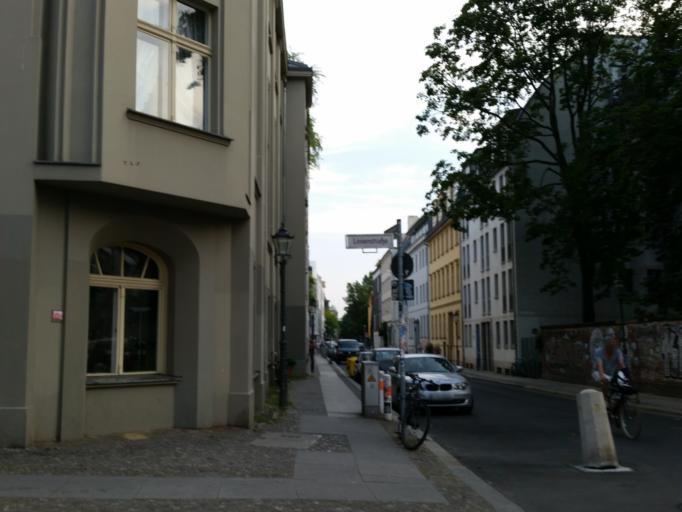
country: DE
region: Berlin
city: Berlin
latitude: 52.5288
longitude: 13.4053
